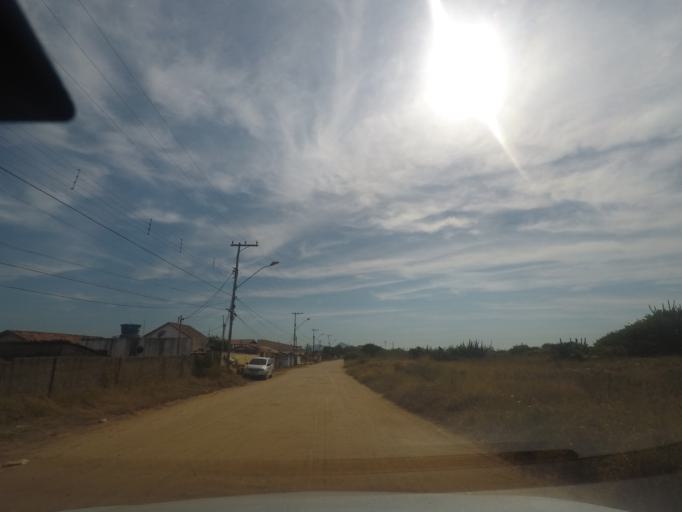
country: BR
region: Rio de Janeiro
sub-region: Marica
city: Marica
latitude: -22.9598
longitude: -42.8369
